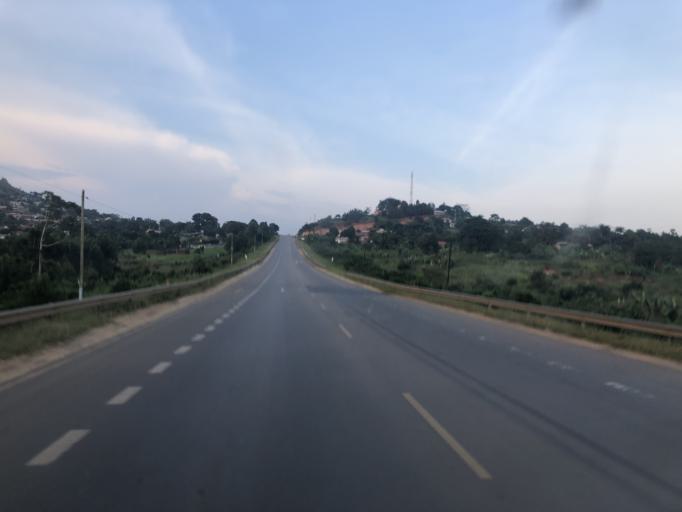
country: UG
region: Central Region
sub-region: Mpigi District
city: Mpigi
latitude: 0.2139
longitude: 32.3252
